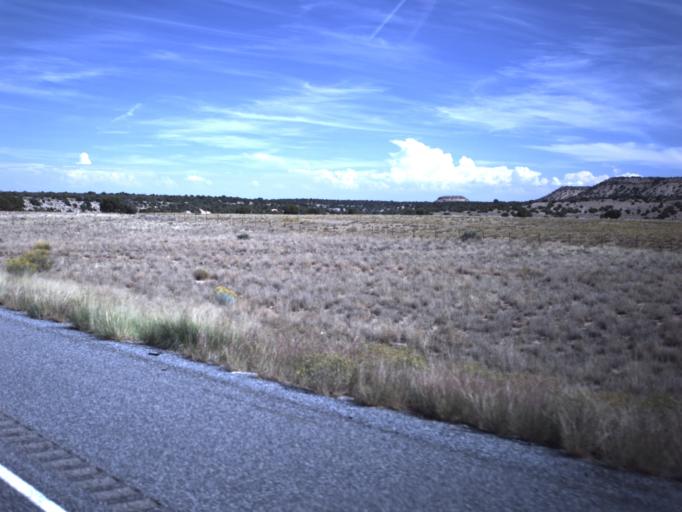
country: US
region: Utah
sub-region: Emery County
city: Castle Dale
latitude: 38.9029
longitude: -110.5611
